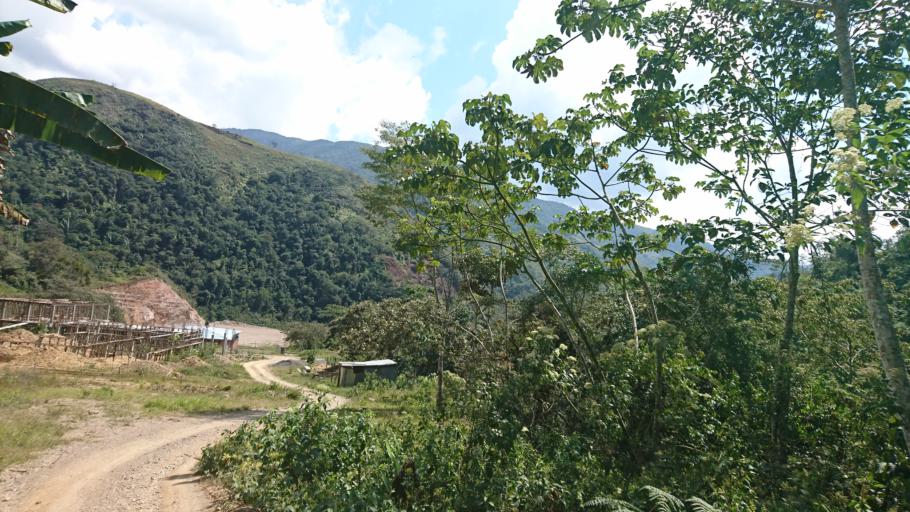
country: BO
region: La Paz
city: Coroico
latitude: -16.0400
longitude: -67.8142
